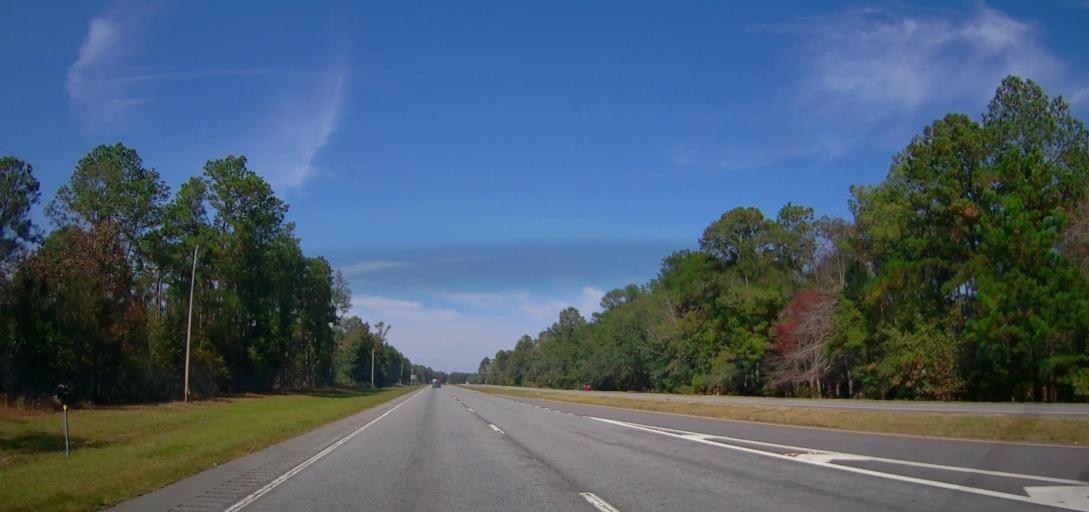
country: US
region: Georgia
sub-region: Lee County
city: Leesburg
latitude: 31.7387
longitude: -83.9866
